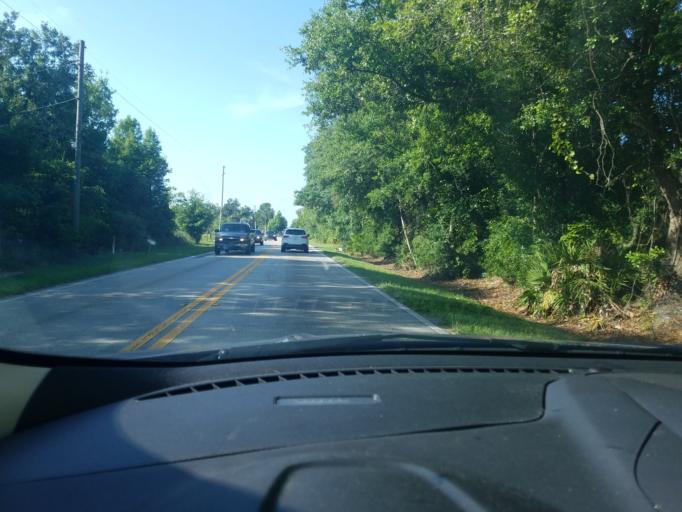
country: US
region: Florida
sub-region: Osceola County
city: Buenaventura Lakes
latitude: 28.3553
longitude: -81.3097
